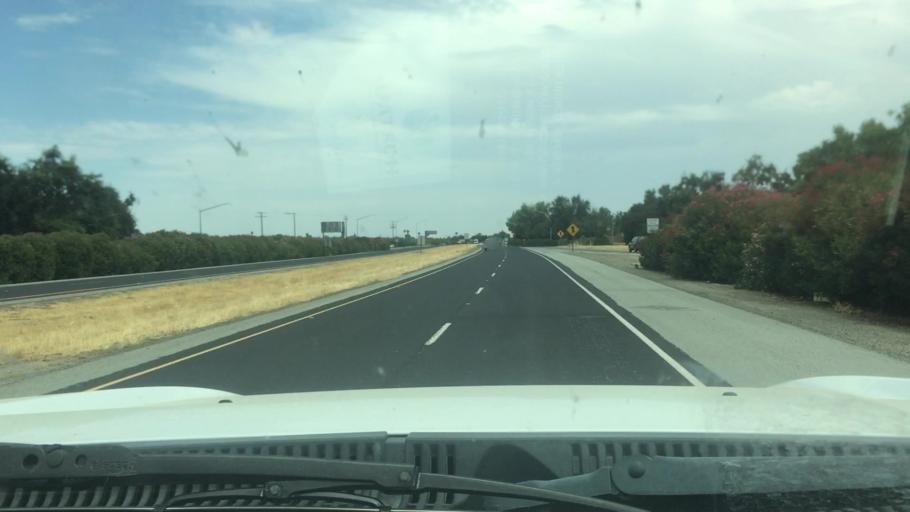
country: US
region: California
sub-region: Tulare County
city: Porterville
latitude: 36.0522
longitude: -119.0389
